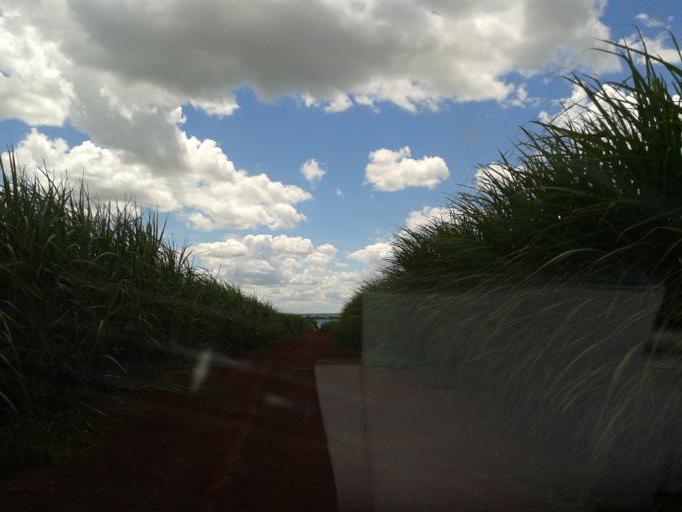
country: BR
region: Minas Gerais
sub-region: Santa Vitoria
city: Santa Vitoria
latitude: -18.6923
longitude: -50.1899
